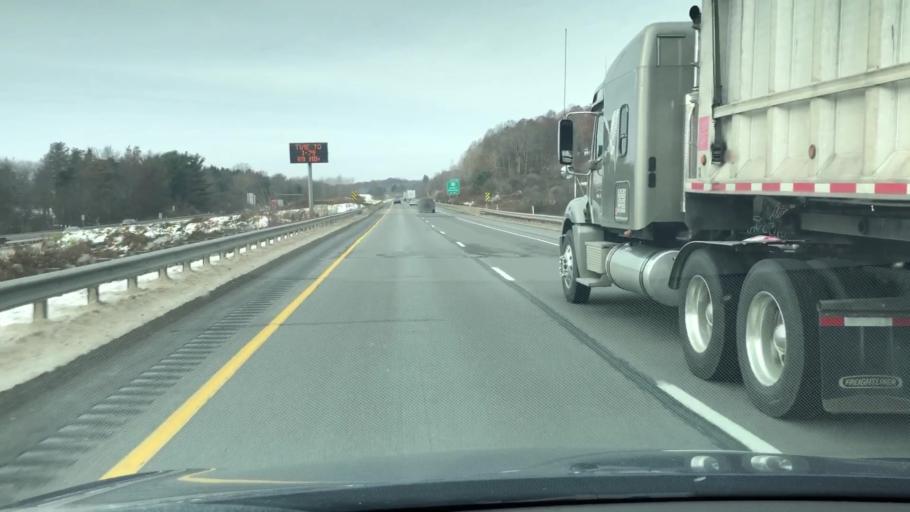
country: US
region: Pennsylvania
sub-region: Clearfield County
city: DuBois
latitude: 41.1418
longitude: -78.7449
